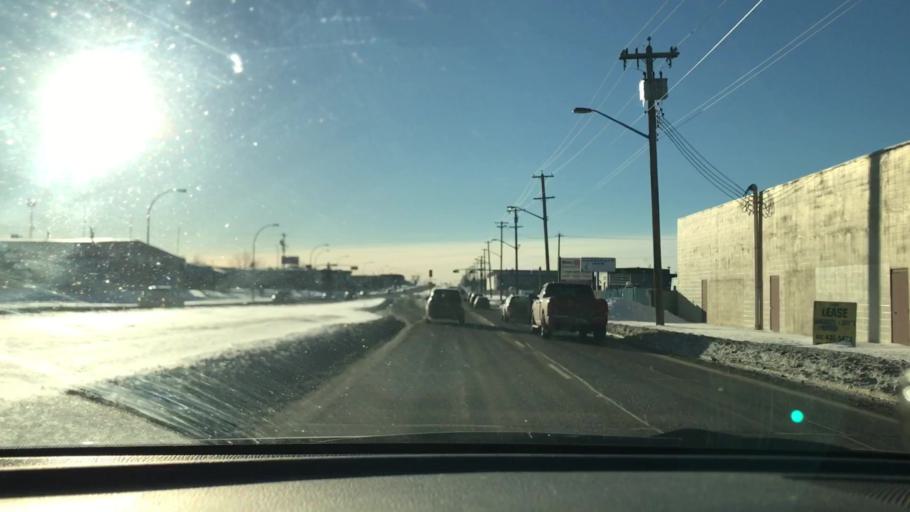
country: CA
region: Alberta
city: Edmonton
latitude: 53.4954
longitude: -113.4673
